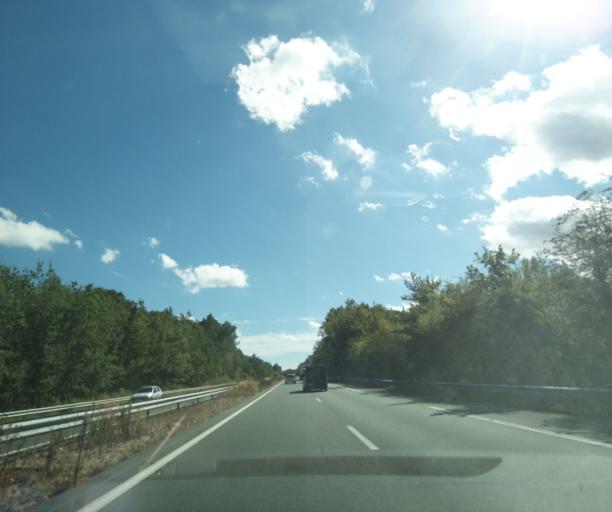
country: FR
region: Aquitaine
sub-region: Departement du Lot-et-Garonne
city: Fourques-sur-Garonne
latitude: 44.3971
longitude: 0.1917
